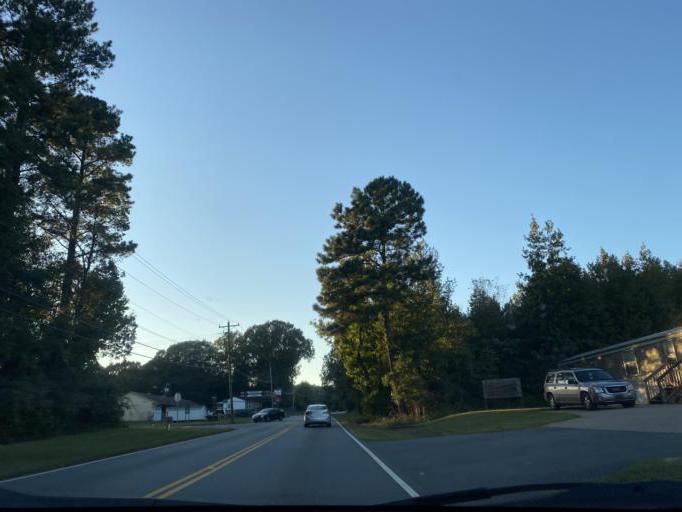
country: US
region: South Carolina
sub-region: Cherokee County
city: Gaffney
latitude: 35.0901
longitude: -81.6501
